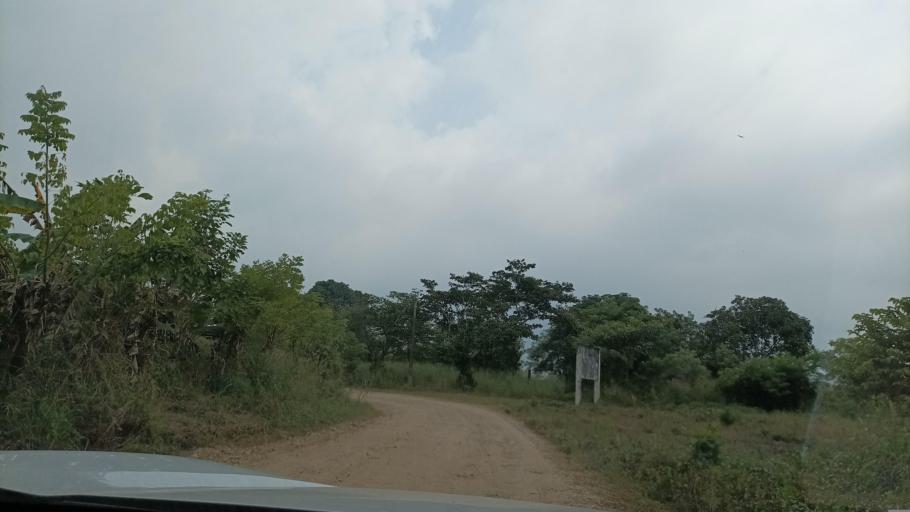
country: MX
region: Veracruz
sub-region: Moloacan
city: Cuichapa
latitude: 17.5798
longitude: -94.2231
